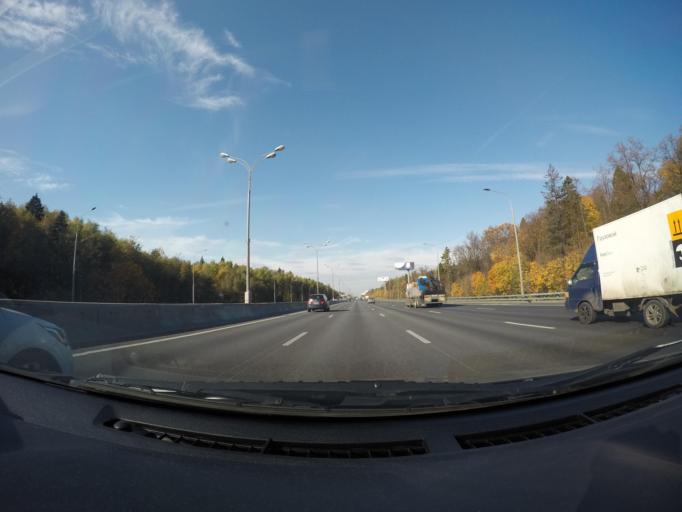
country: RU
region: Moscow
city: Gol'yanovo
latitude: 55.8434
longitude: 37.8020
